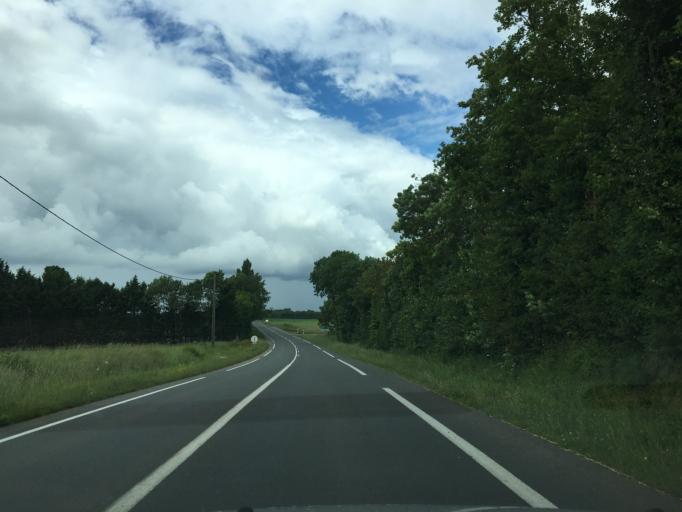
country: FR
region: Poitou-Charentes
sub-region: Departement de la Charente-Maritime
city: Saint-Jean-d'Angely
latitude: 46.0529
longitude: -0.5101
